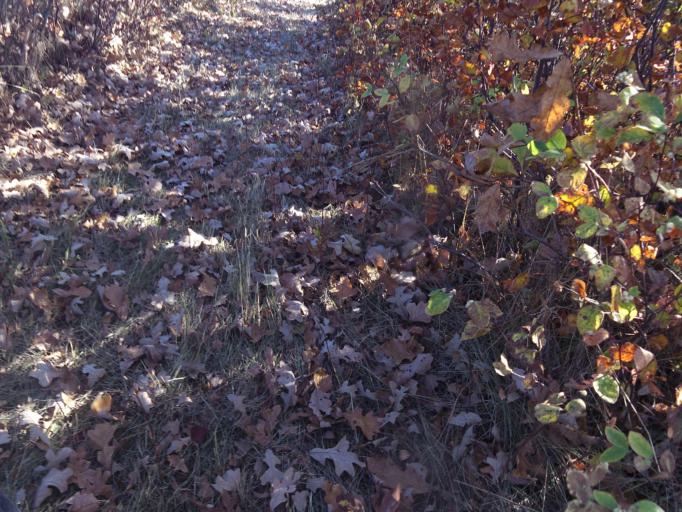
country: CA
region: Manitoba
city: Morden
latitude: 48.9464
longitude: -98.0750
